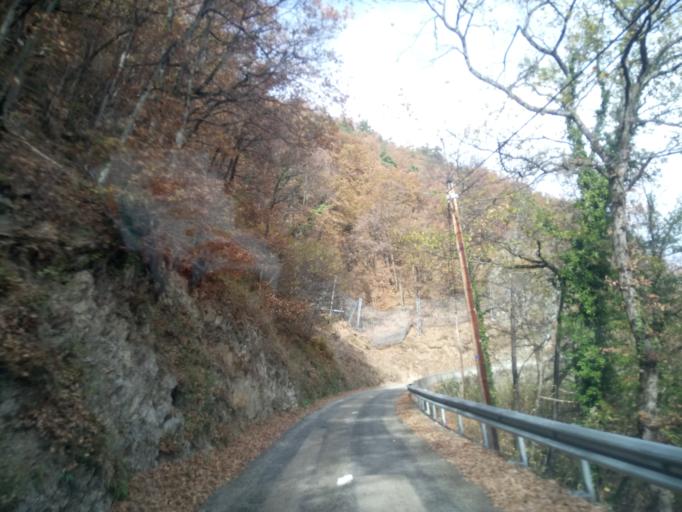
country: FR
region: Rhone-Alpes
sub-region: Departement de la Savoie
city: La Chambre
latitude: 45.3786
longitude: 6.3088
